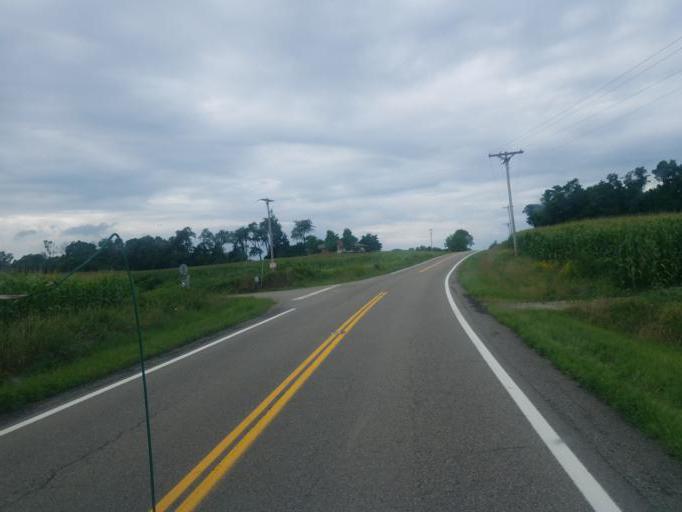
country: US
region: Ohio
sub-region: Knox County
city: Oak Hill
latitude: 40.4316
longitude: -82.1422
